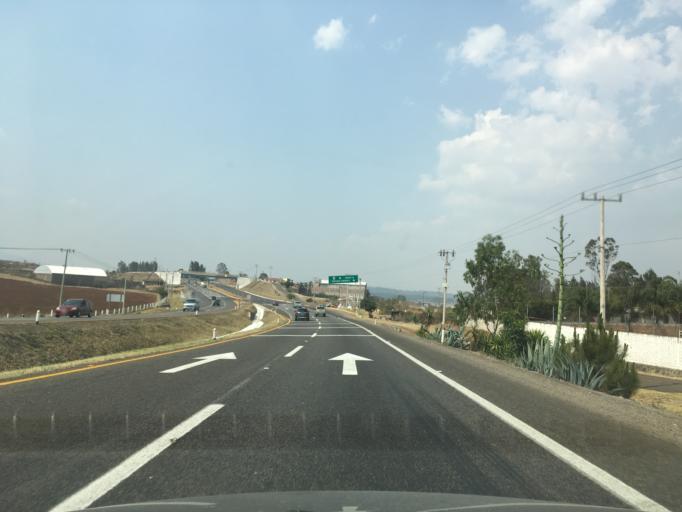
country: MX
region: Michoacan
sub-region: Morelia
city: La Mintzita (Piedra Dura)
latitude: 19.5982
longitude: -101.2920
